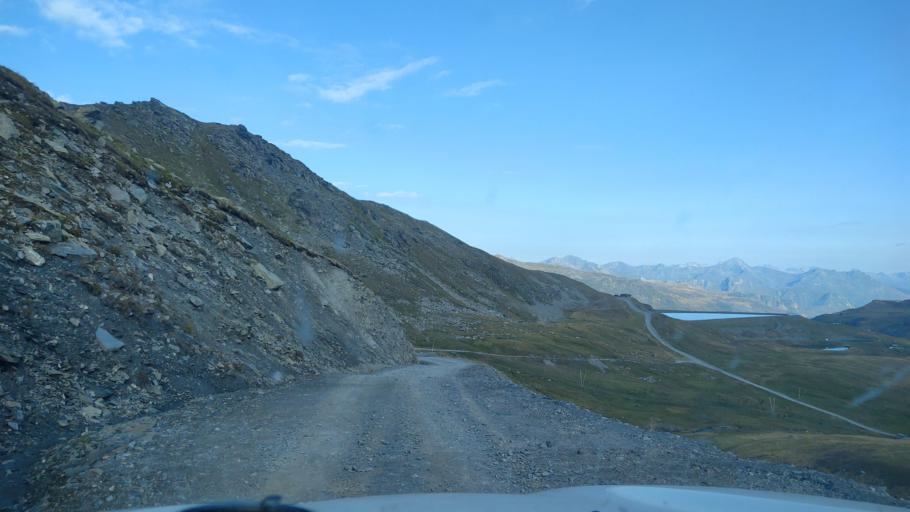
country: FR
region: Rhone-Alpes
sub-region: Departement de la Savoie
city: Val Thorens
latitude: 45.2801
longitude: 6.5861
